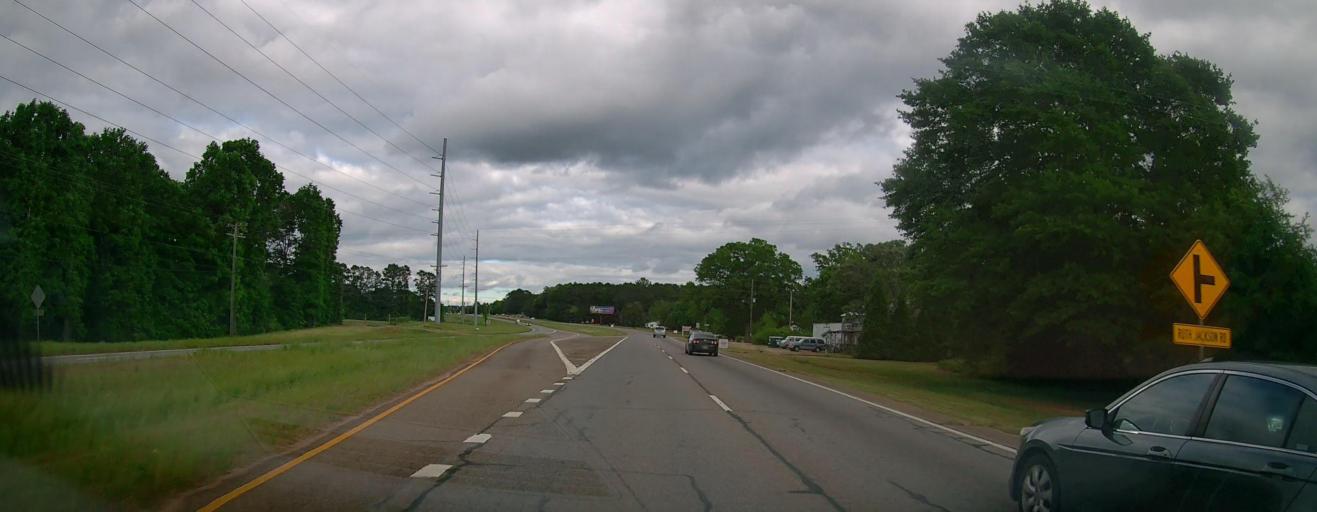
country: US
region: Georgia
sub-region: Oconee County
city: Bogart
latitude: 33.9183
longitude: -83.5274
